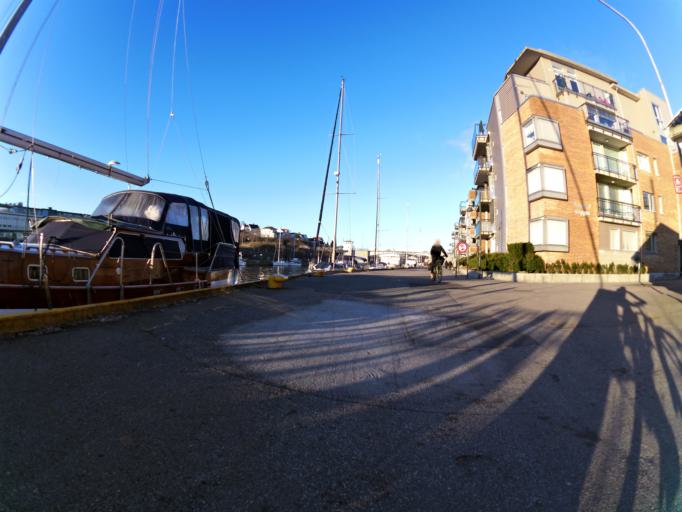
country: NO
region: Ostfold
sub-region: Fredrikstad
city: Fredrikstad
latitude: 59.2062
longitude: 10.9405
